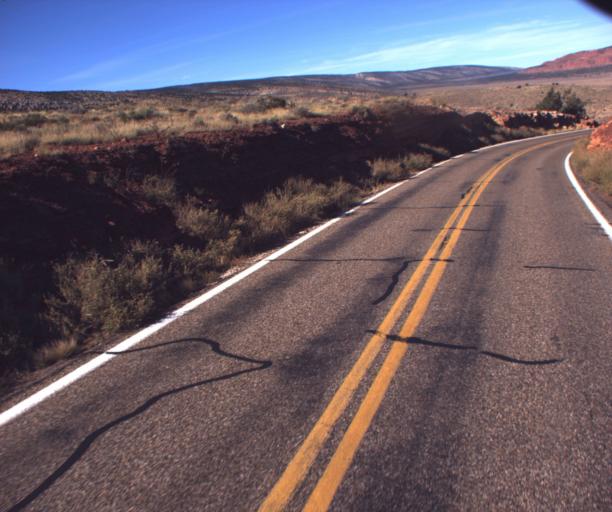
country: US
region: Arizona
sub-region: Coconino County
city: Fredonia
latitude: 36.7296
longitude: -112.0621
